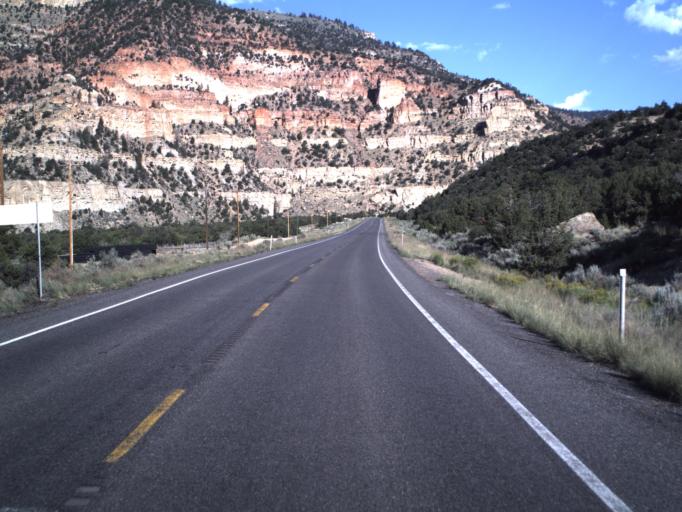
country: US
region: Utah
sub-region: Emery County
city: Huntington
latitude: 39.3937
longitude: -111.1014
